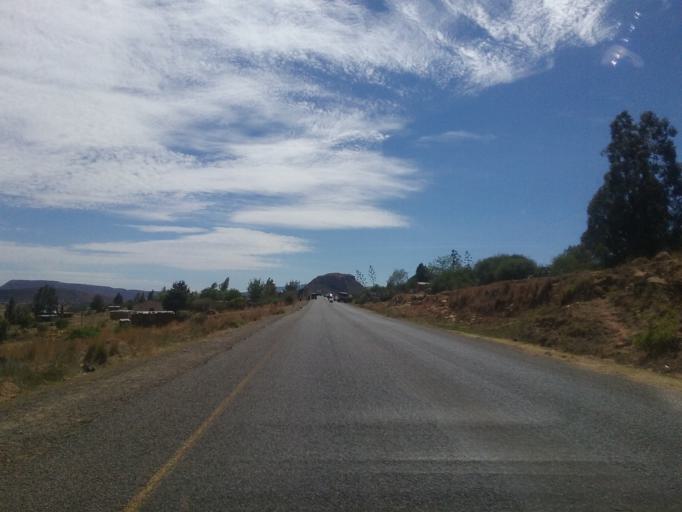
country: LS
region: Mohale's Hoek District
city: Mohale's Hoek
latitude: -30.1832
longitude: 27.4251
